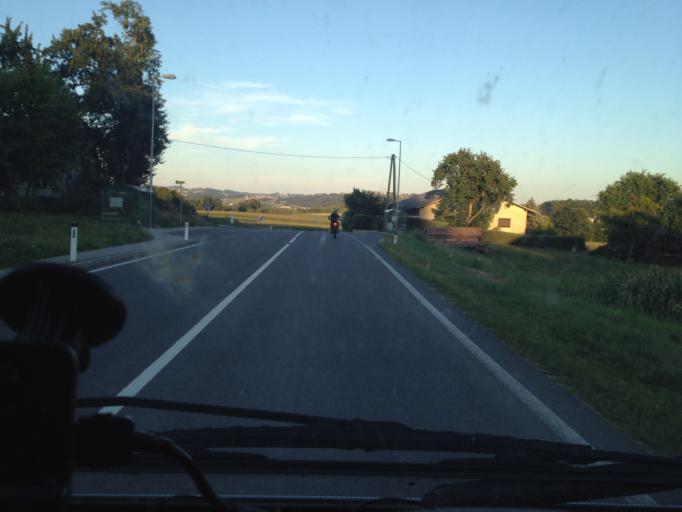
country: AT
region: Upper Austria
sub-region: Politischer Bezirk Urfahr-Umgebung
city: Engerwitzdorf
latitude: 48.3625
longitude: 14.4455
